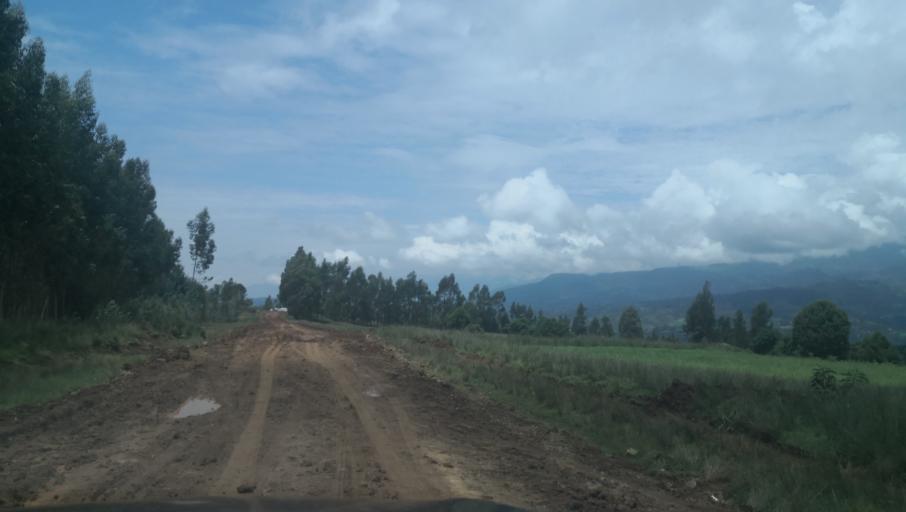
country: ET
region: Southern Nations, Nationalities, and People's Region
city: Butajira
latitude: 8.2850
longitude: 38.4701
